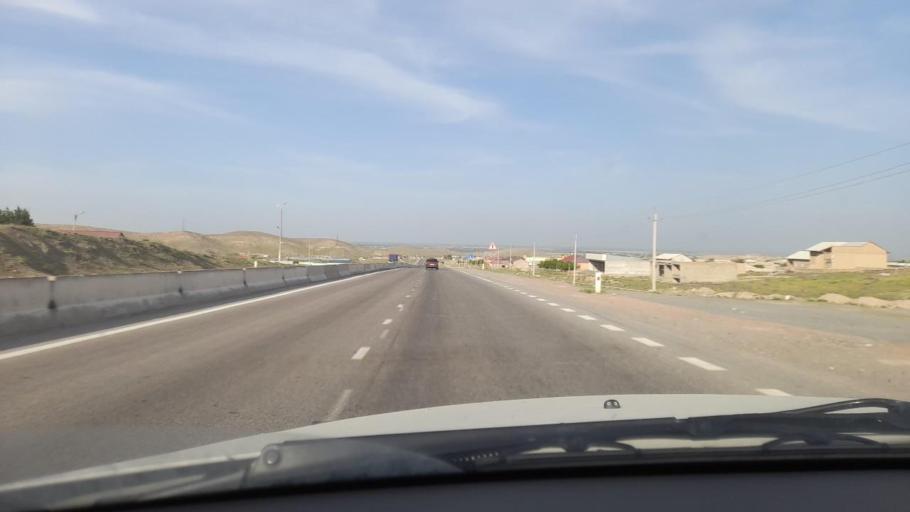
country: UZ
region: Jizzax
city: Jizzax
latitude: 40.0600
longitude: 67.8294
